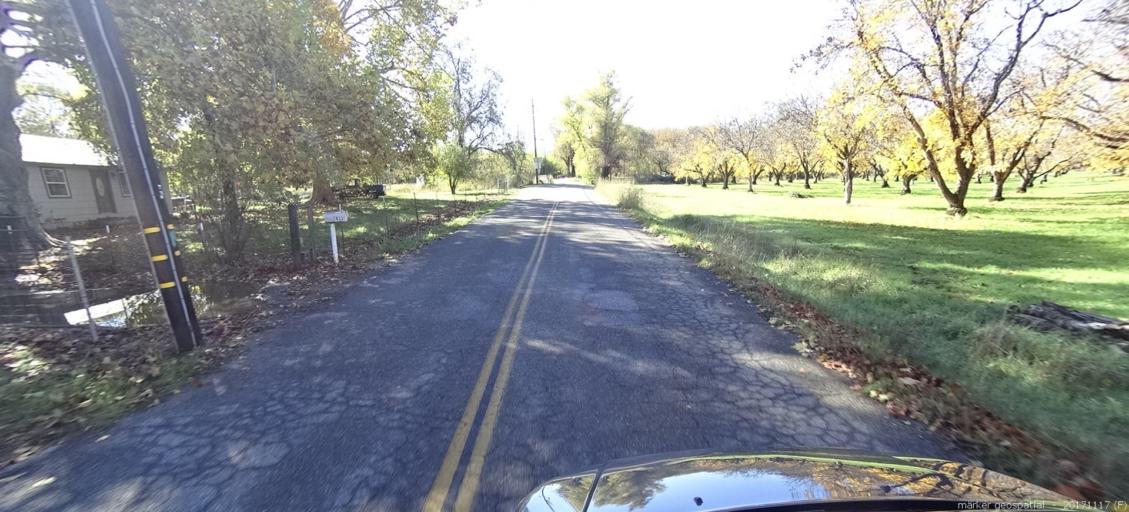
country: US
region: California
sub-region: Shasta County
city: Anderson
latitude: 40.4459
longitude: -122.2422
